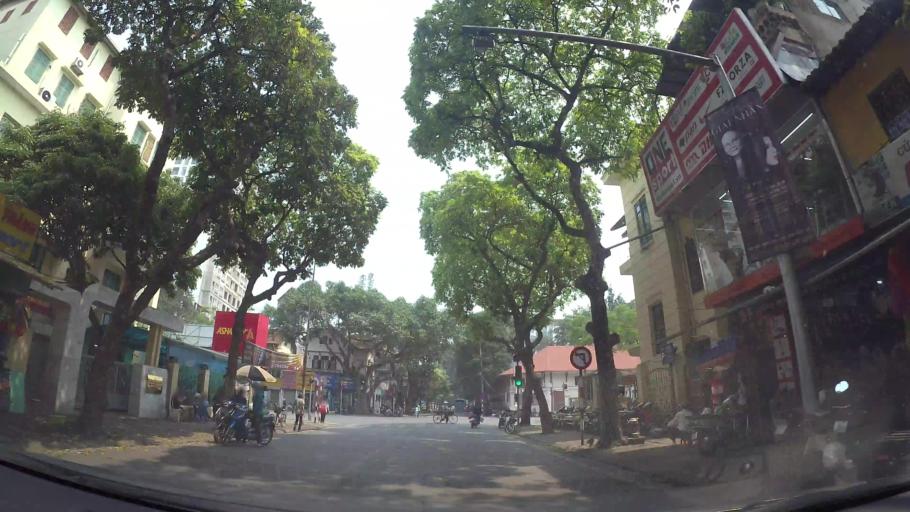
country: VN
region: Ha Noi
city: Hanoi
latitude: 21.0309
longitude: 105.8325
